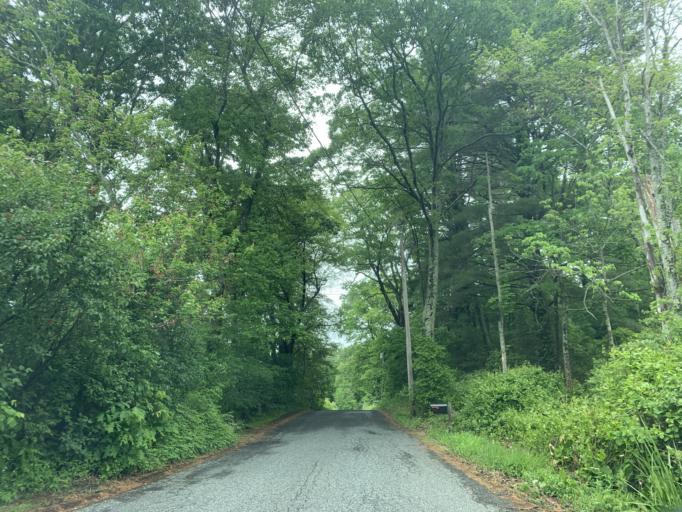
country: US
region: Massachusetts
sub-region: Worcester County
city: Upton
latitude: 42.1860
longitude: -71.6243
